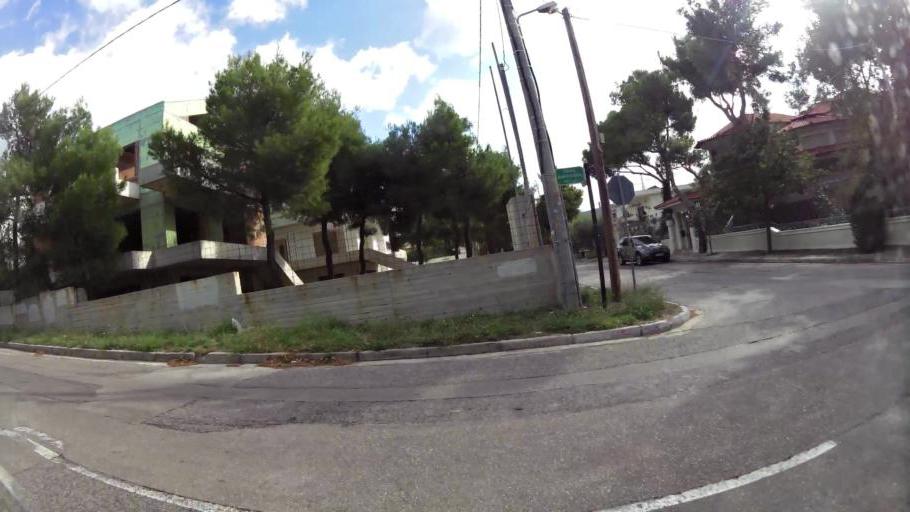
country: GR
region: Attica
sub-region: Nomarchia Anatolikis Attikis
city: Thrakomakedones
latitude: 38.1277
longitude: 23.7507
